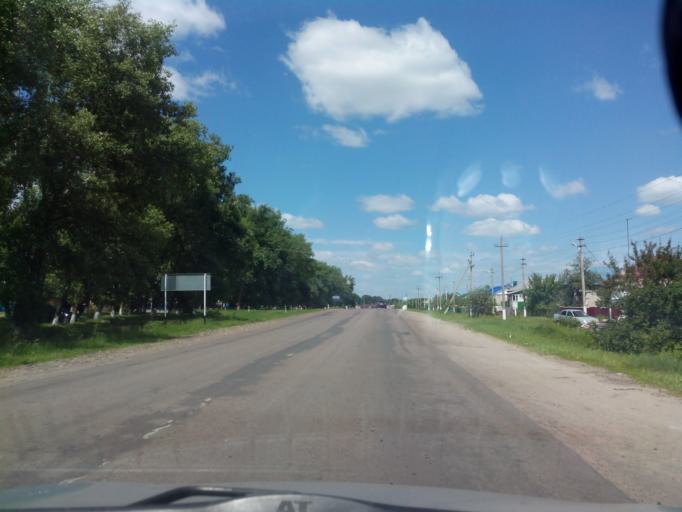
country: RU
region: Voronezj
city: Ternovka
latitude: 51.6721
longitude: 41.5801
